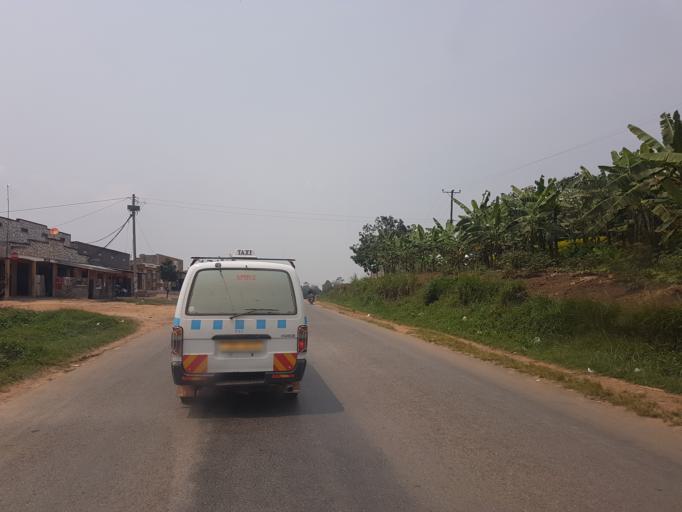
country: UG
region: Western Region
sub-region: Bushenyi District
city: Bushenyi
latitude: -0.5398
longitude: 30.1645
